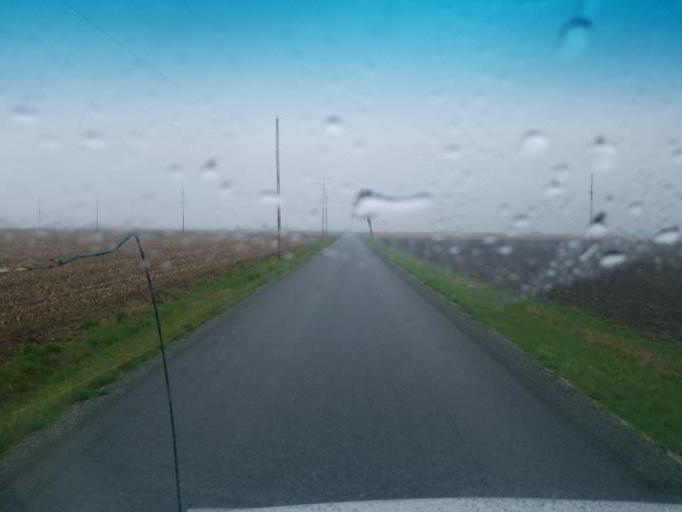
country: US
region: Ohio
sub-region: Wyandot County
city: Carey
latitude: 40.9924
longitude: -83.3372
